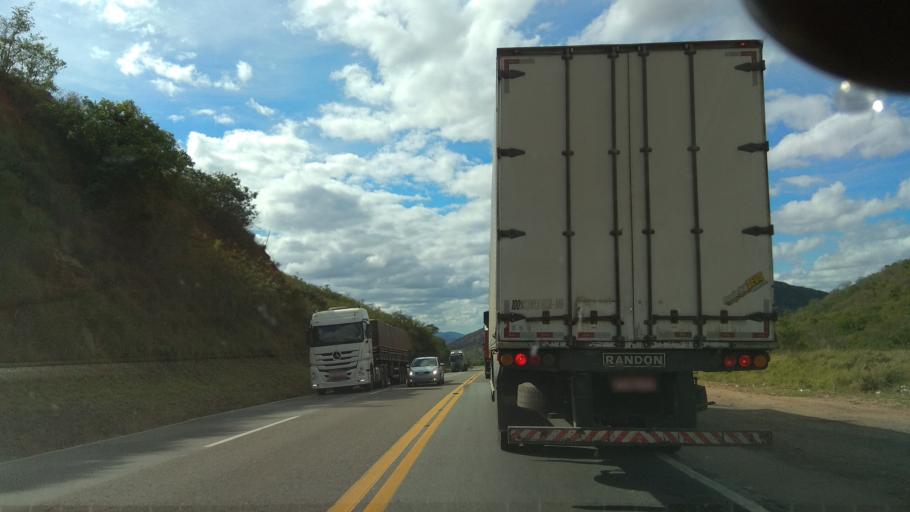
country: BR
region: Bahia
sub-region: Amargosa
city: Amargosa
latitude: -12.8941
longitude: -39.8603
